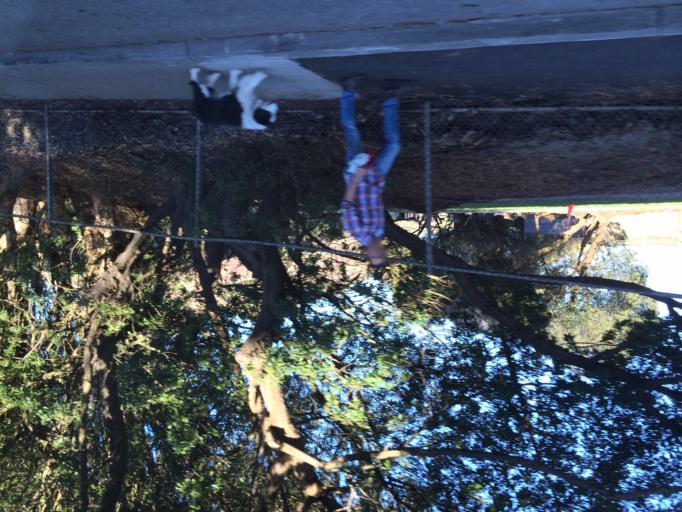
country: US
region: California
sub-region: San Francisco County
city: San Francisco
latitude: 37.7652
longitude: -122.4411
